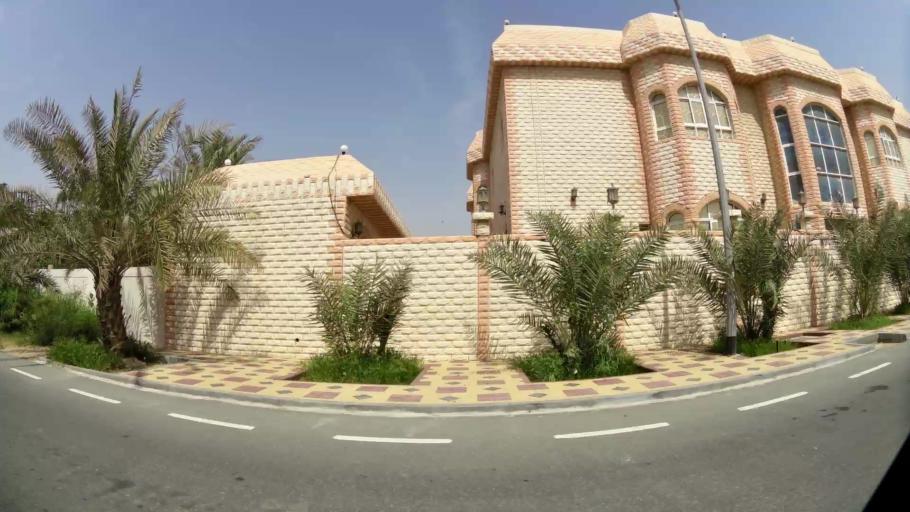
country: AE
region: Ash Shariqah
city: Sharjah
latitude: 25.2341
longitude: 55.4469
